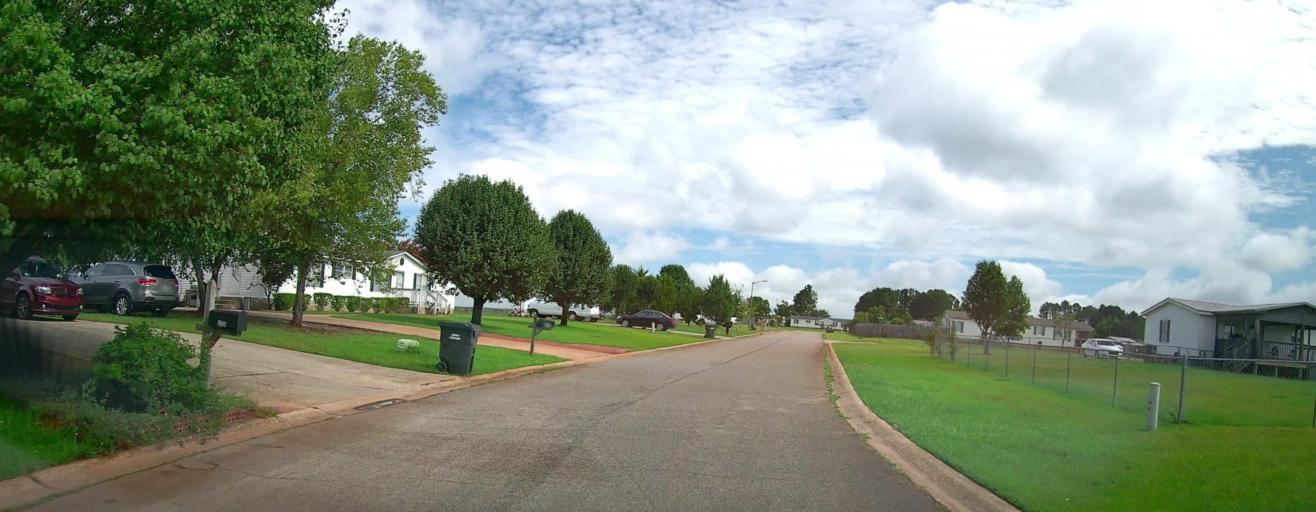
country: US
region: Georgia
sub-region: Houston County
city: Centerville
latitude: 32.6467
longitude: -83.7172
